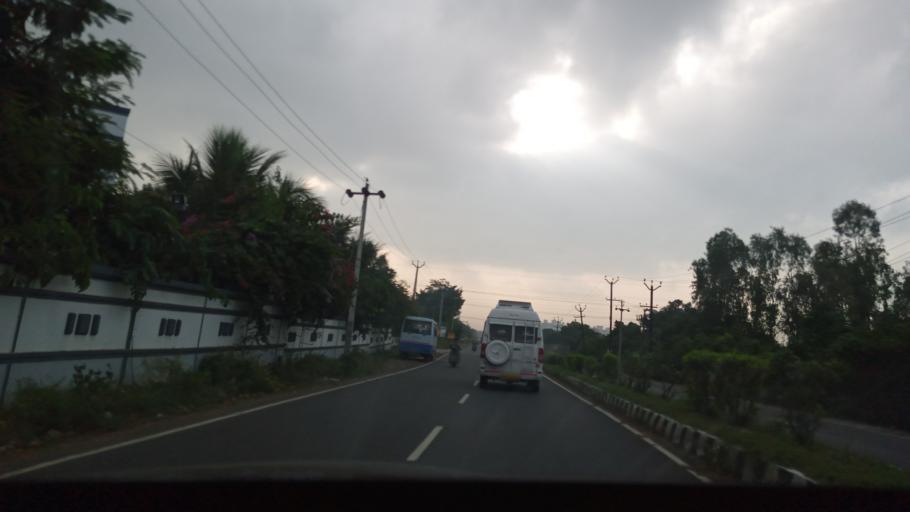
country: IN
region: Tamil Nadu
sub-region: Kancheepuram
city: Vengavasal
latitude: 12.8042
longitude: 80.1914
